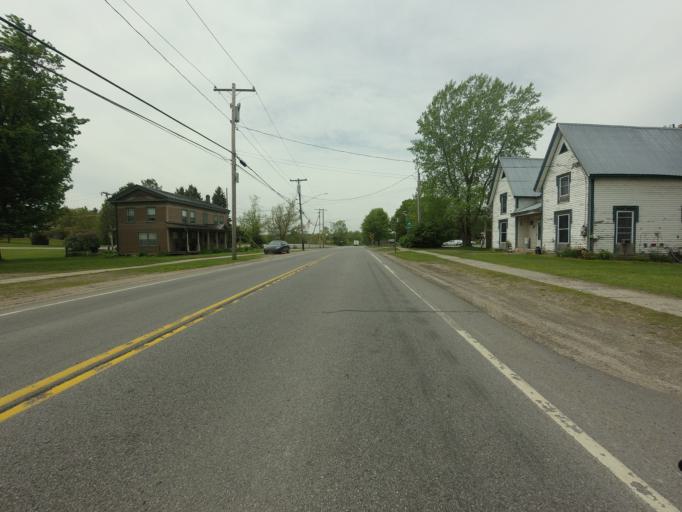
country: US
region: New York
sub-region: St. Lawrence County
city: Hannawa Falls
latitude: 44.6267
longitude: -74.8169
